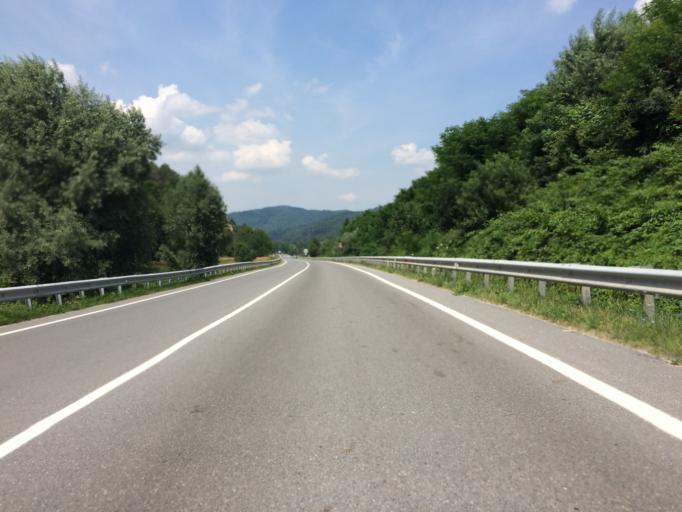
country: IT
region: Piedmont
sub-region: Provincia di Cuneo
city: Robilante
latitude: 44.2670
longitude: 7.5186
